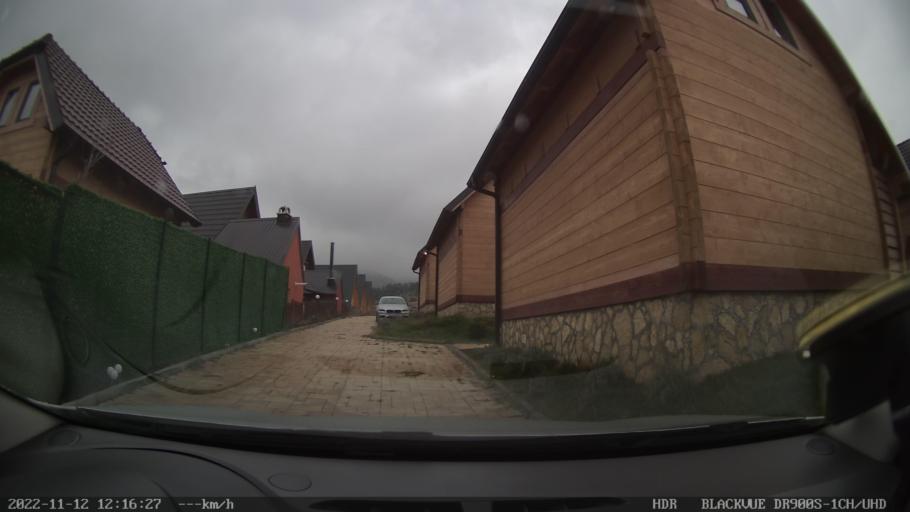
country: RS
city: Zlatibor
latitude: 43.7034
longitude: 19.7249
